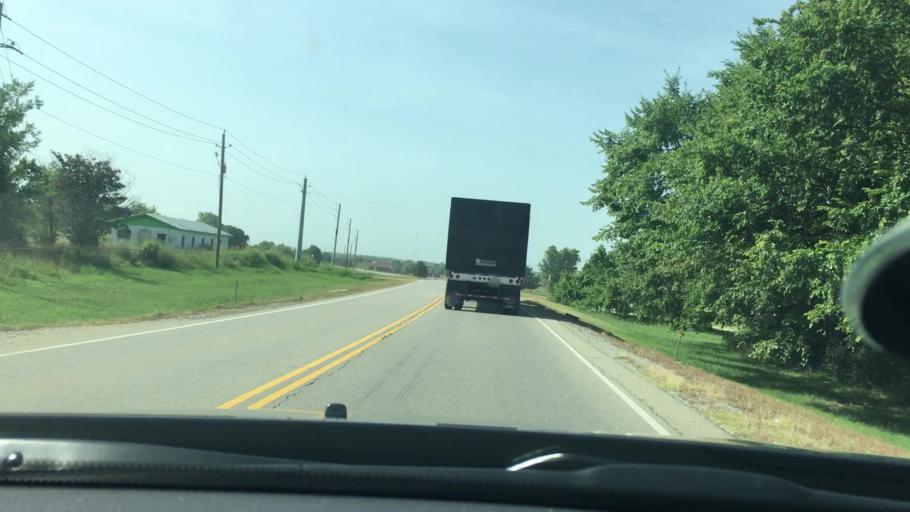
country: US
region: Oklahoma
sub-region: Coal County
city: Coalgate
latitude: 34.4661
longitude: -96.2173
